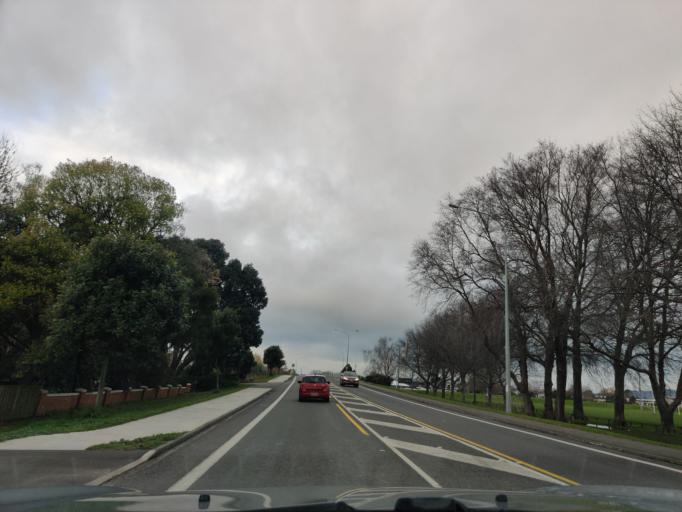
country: NZ
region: Hawke's Bay
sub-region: Napier City
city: Taradale
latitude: -39.5799
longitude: 176.9146
